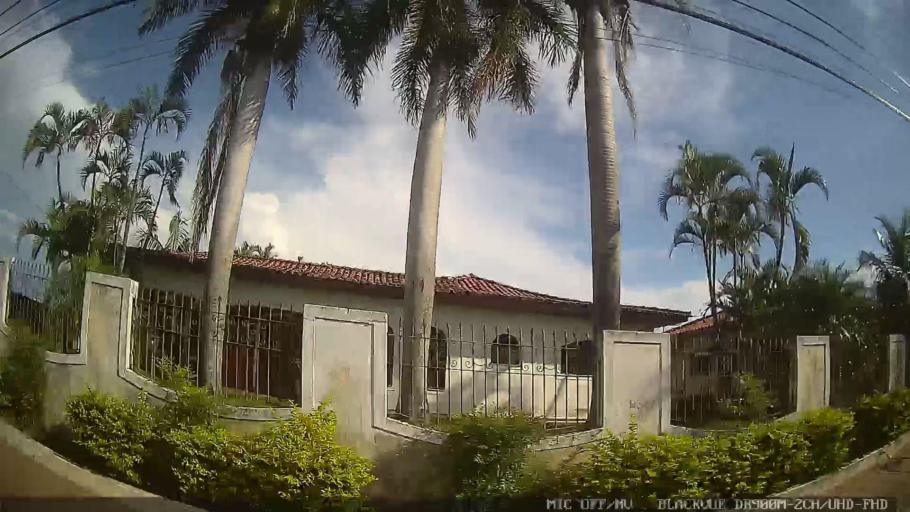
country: BR
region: Sao Paulo
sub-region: Laranjal Paulista
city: Laranjal Paulista
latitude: -23.0846
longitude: -47.7902
